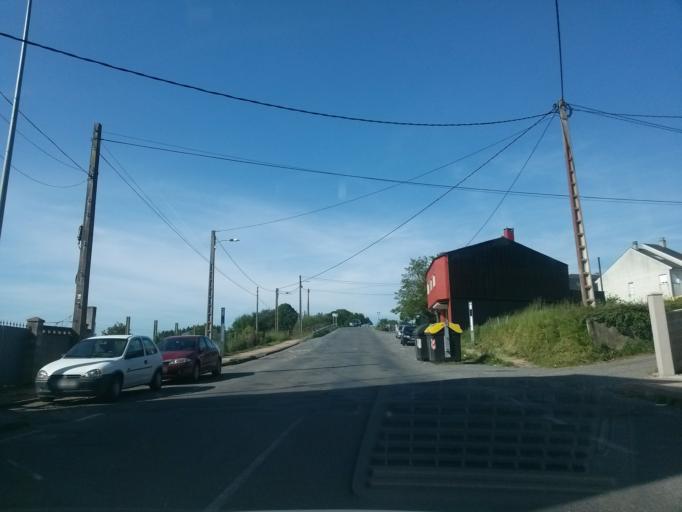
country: ES
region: Galicia
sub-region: Provincia de Lugo
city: Lugo
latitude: 43.0319
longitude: -7.5591
